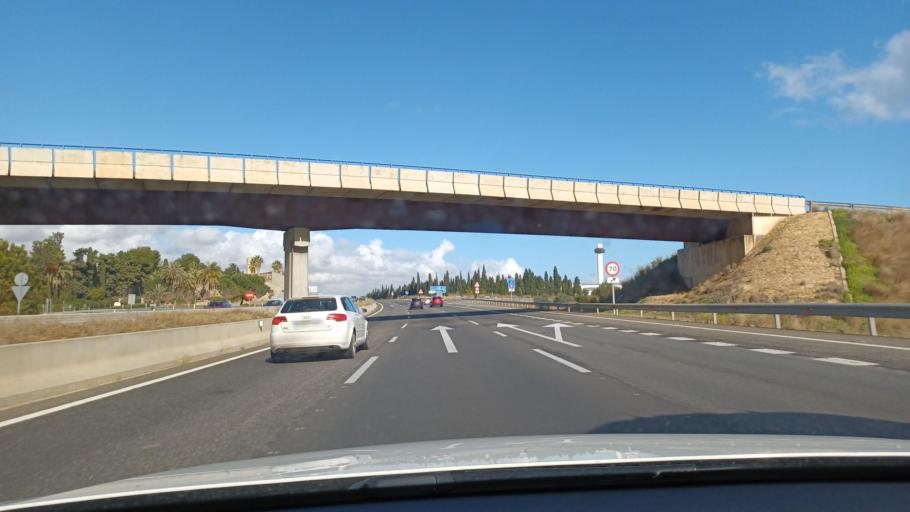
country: ES
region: Valencia
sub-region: Provincia de Valencia
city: Benifaio
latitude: 39.3112
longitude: -0.4422
